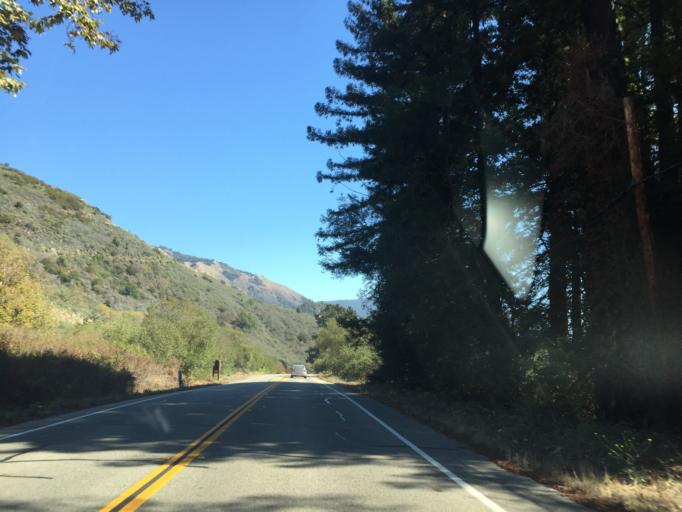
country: US
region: California
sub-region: Monterey County
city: Greenfield
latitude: 36.0194
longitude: -121.5392
